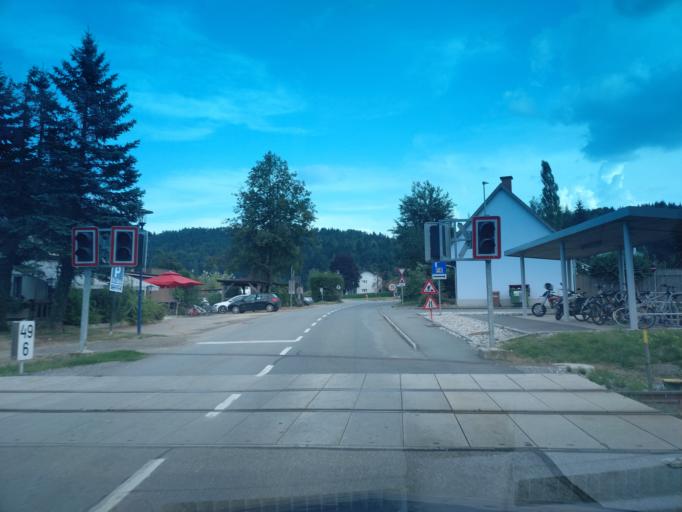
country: AT
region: Styria
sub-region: Politischer Bezirk Deutschlandsberg
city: Wies
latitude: 46.7184
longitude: 15.2727
